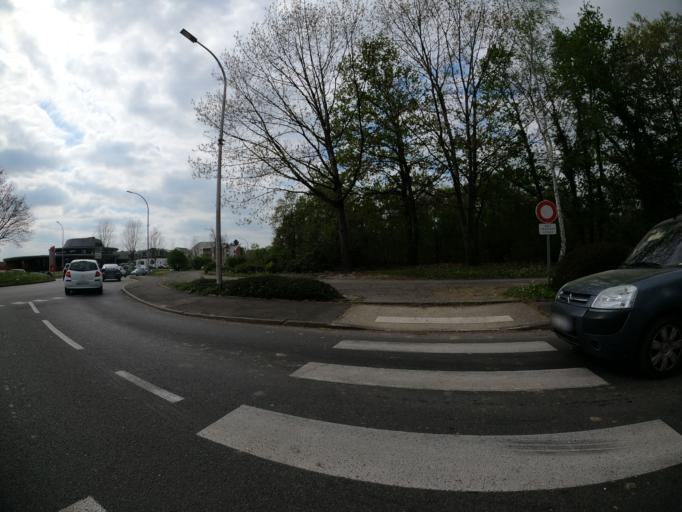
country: FR
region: Aquitaine
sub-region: Departement des Pyrenees-Atlantiques
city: Lons
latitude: 43.3211
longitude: -0.3917
